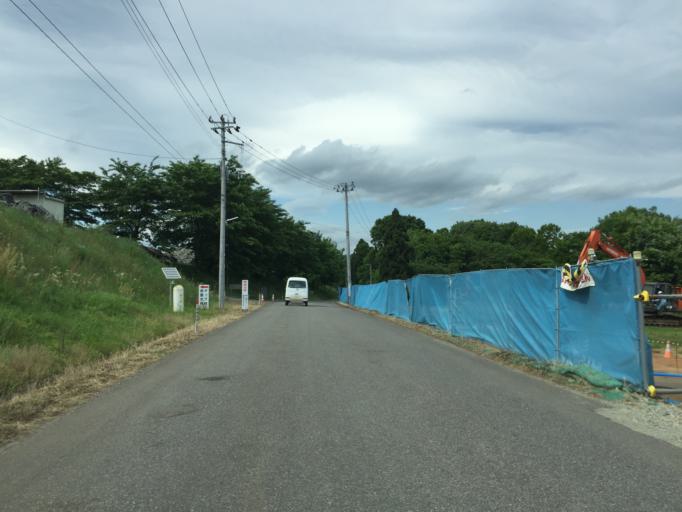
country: JP
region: Fukushima
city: Nihommatsu
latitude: 37.6434
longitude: 140.5259
